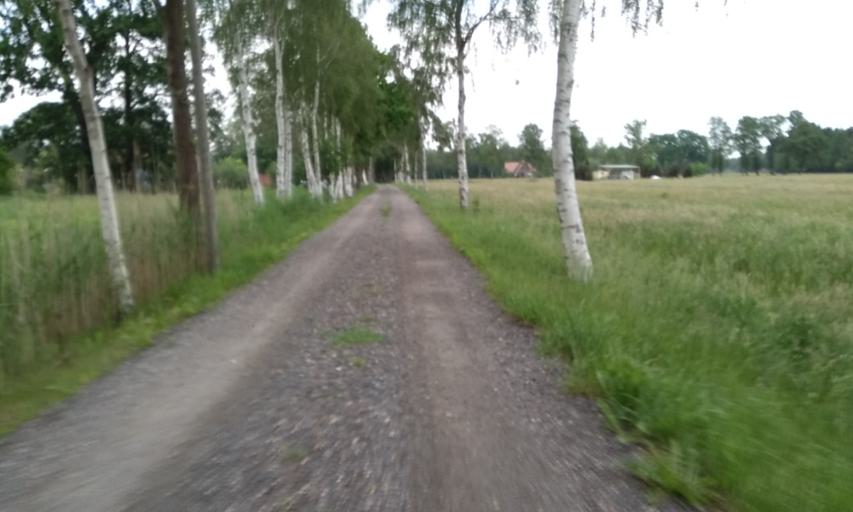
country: DE
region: Lower Saxony
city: Buxtehude
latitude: 53.4875
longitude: 9.6774
